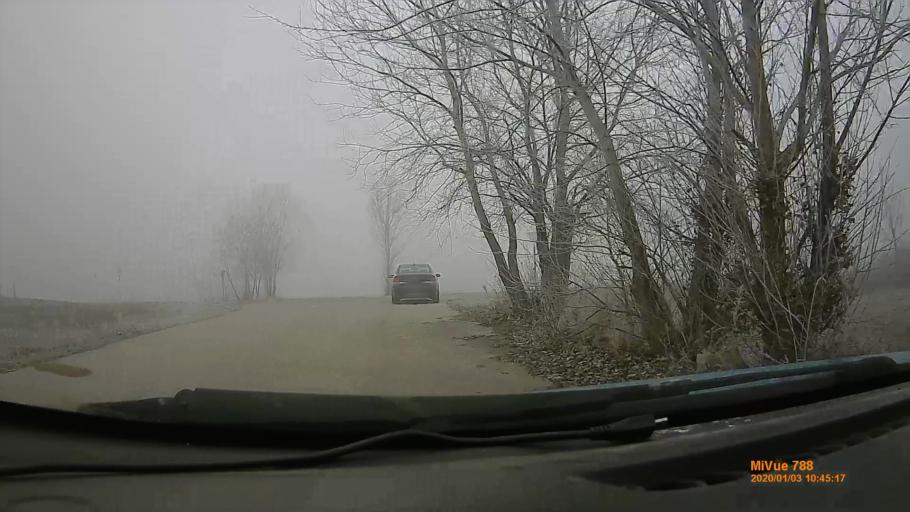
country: HU
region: Tolna
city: Bataszek
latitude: 46.2055
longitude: 18.7151
